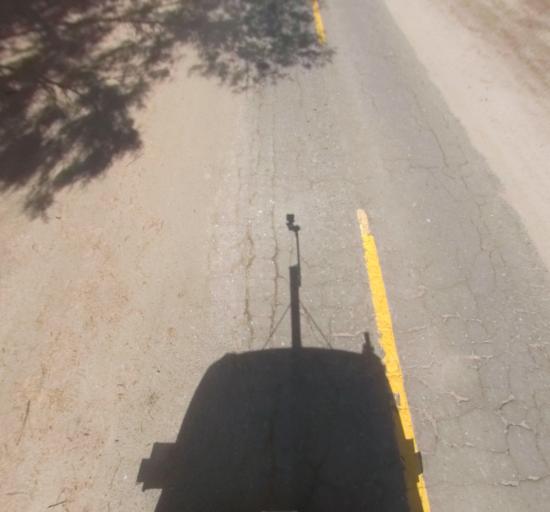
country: US
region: California
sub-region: Madera County
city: Chowchilla
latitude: 37.0325
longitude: -120.3892
